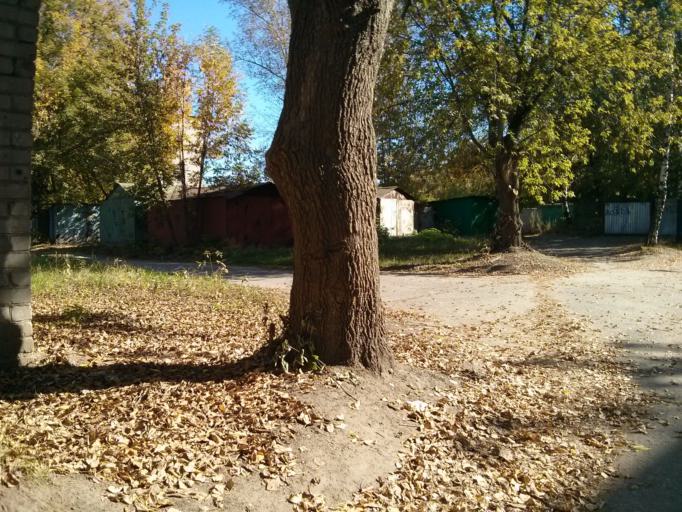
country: RU
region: Vladimir
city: Murom
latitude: 55.5509
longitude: 42.0570
